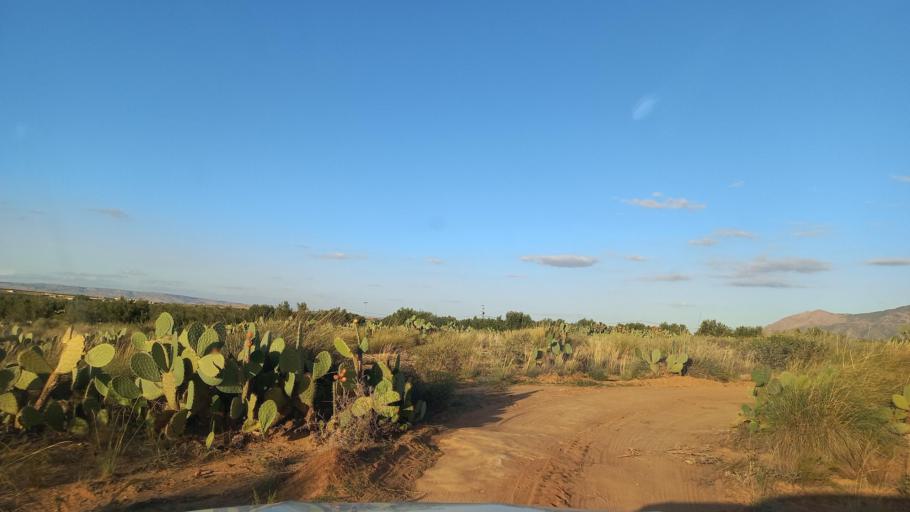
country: TN
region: Al Qasrayn
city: Sbiba
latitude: 35.4207
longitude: 9.1300
